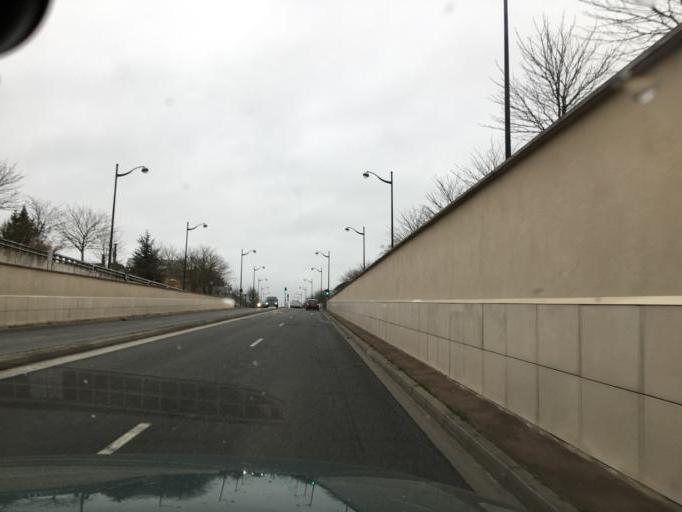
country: FR
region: Centre
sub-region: Departement du Loiret
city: Saint-Jean-le-Blanc
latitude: 47.9085
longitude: 1.9226
